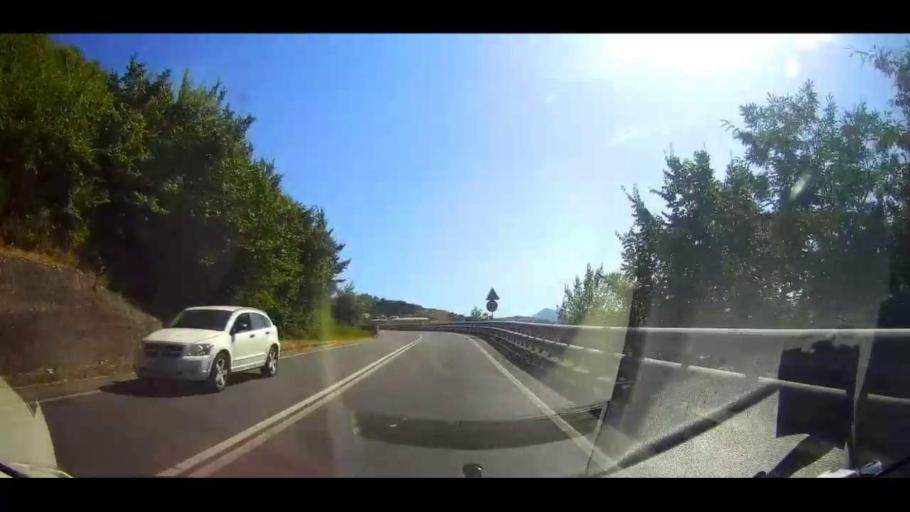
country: IT
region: Calabria
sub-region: Provincia di Cosenza
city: Cosenza
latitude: 39.2993
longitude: 16.2649
